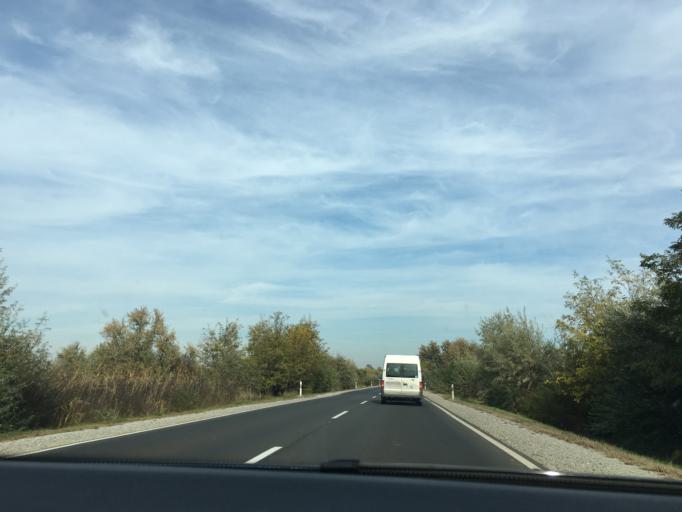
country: HU
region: Szabolcs-Szatmar-Bereg
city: Ujfeherto
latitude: 47.7863
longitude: 21.6919
